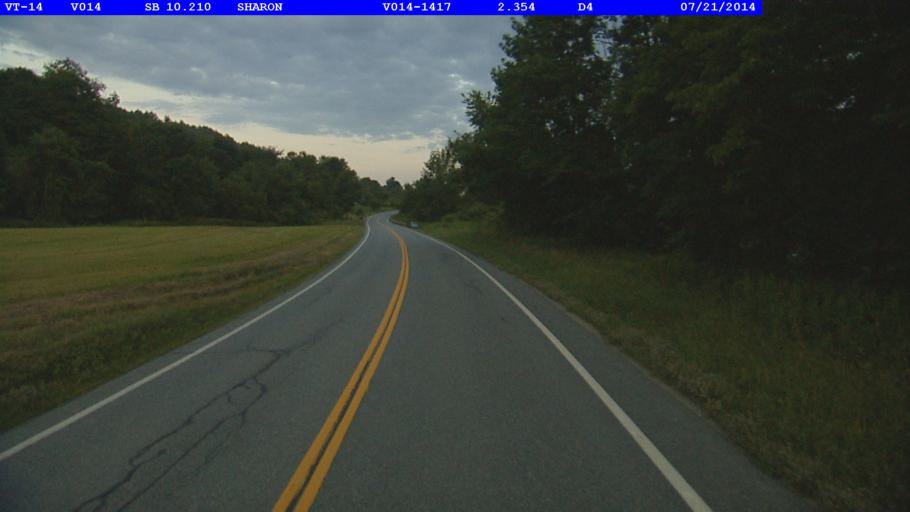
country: US
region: Vermont
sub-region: Windsor County
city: Woodstock
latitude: 43.7506
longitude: -72.4481
